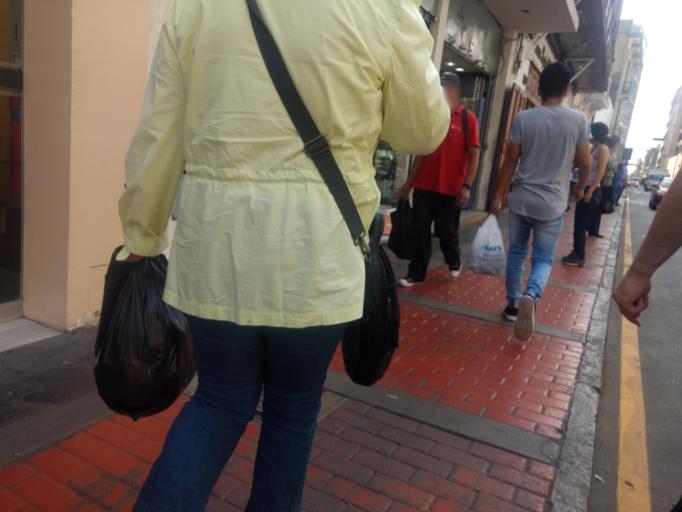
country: PE
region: Lima
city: Lima
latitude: -12.0465
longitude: -77.0352
